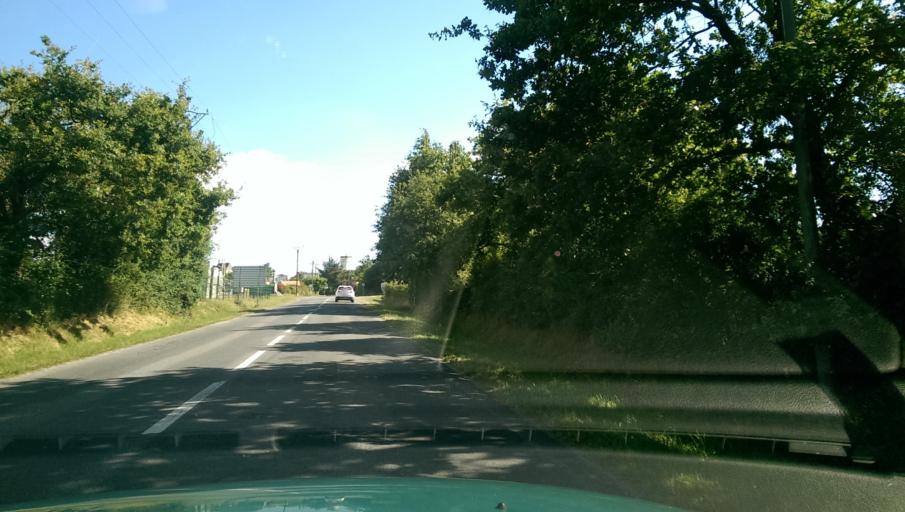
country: FR
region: Pays de la Loire
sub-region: Departement de la Loire-Atlantique
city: Lege
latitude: 46.8905
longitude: -1.6010
